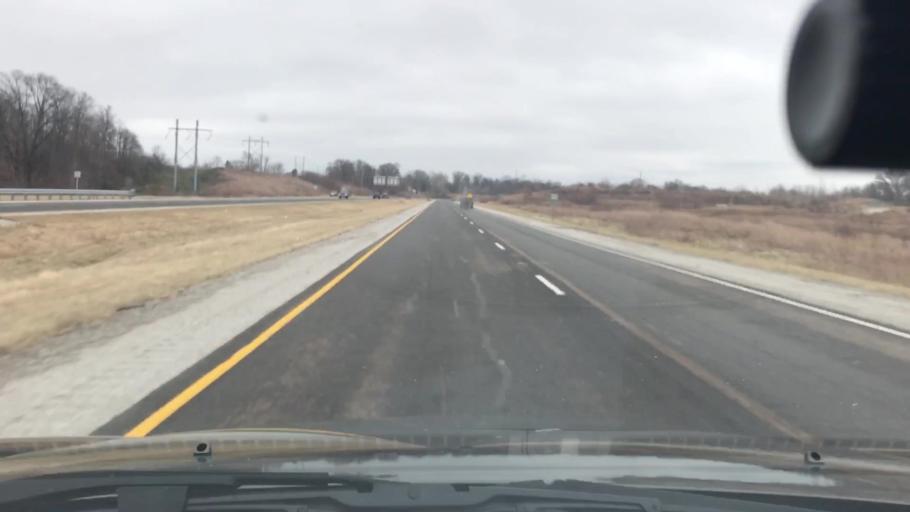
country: US
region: Illinois
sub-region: Madison County
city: Roxana
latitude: 38.8700
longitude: -90.0592
